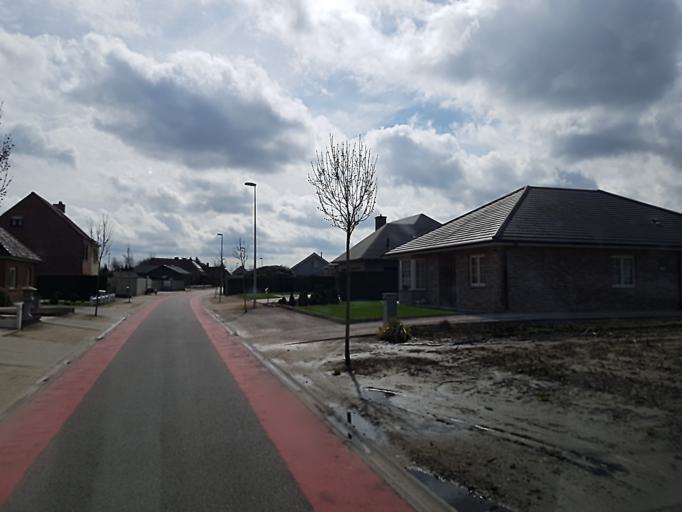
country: BE
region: Flanders
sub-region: Provincie Oost-Vlaanderen
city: Deinze
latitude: 50.9512
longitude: 3.4925
